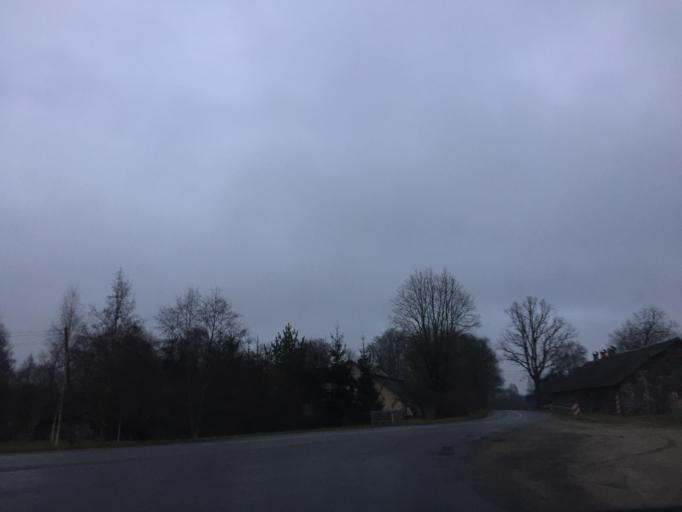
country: LV
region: Koceni
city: Koceni
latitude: 57.5505
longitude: 25.3772
